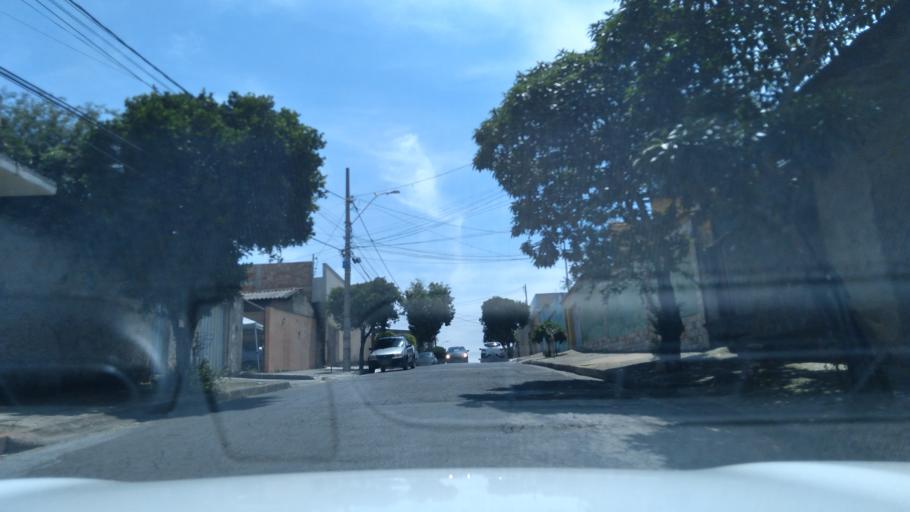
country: BR
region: Minas Gerais
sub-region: Contagem
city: Contagem
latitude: -19.9025
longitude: -44.0156
